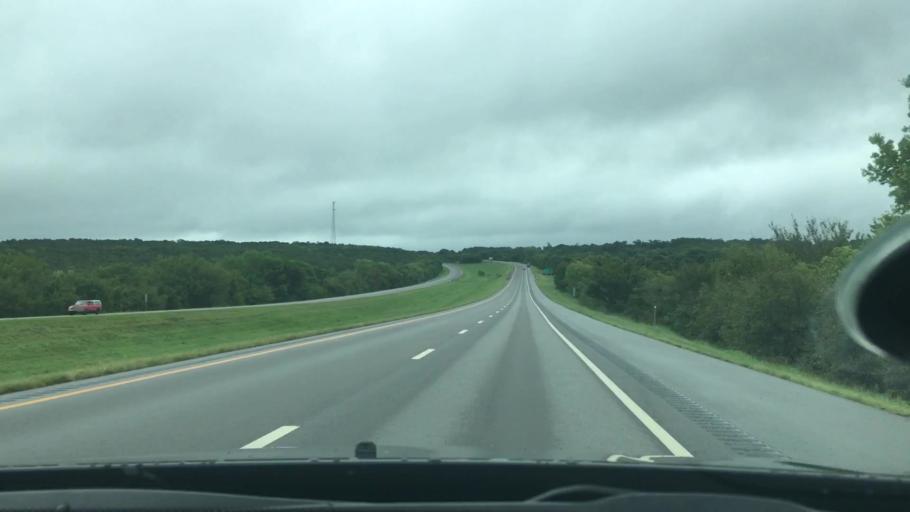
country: US
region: Oklahoma
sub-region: Okmulgee County
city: Henryetta
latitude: 35.4355
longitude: -95.8214
